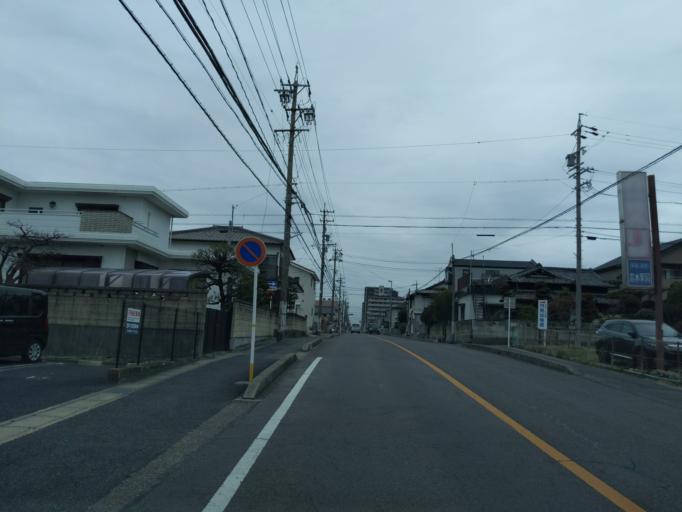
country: JP
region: Aichi
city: Kasugai
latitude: 35.2418
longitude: 136.9752
